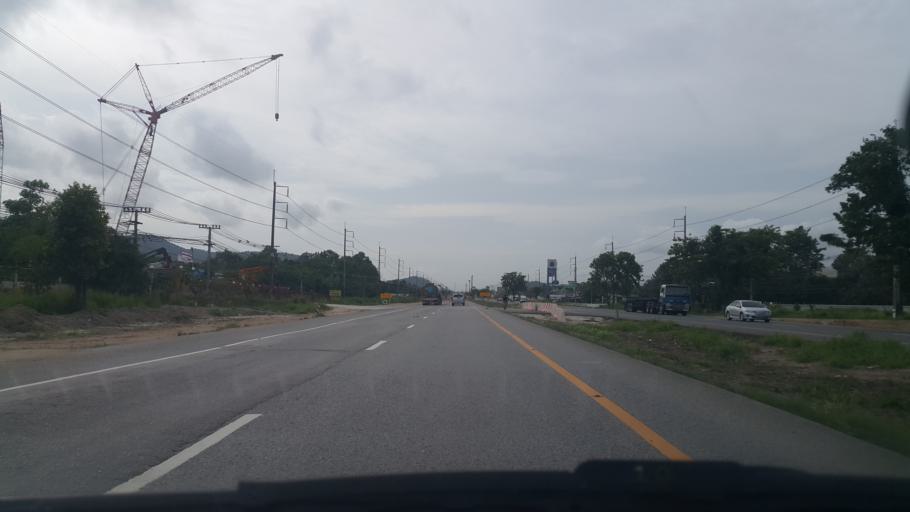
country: TH
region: Rayong
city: Nikhom Phattana
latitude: 12.8042
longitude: 101.1457
